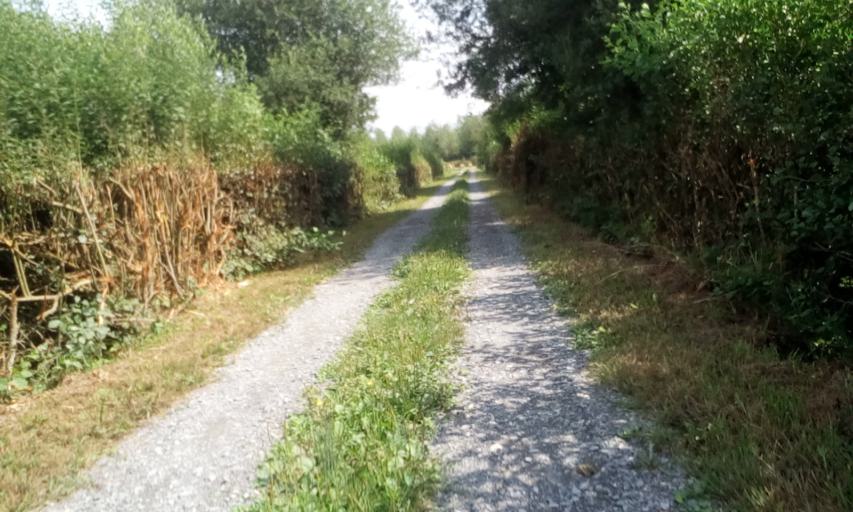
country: FR
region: Lower Normandy
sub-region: Departement du Calvados
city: Bavent
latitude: 49.2384
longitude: -0.1647
